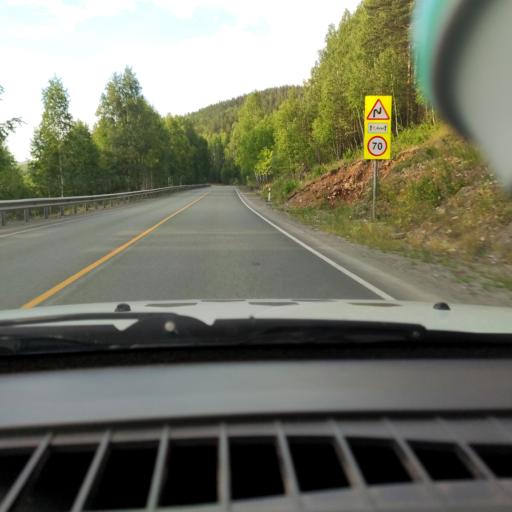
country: RU
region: Chelyabinsk
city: Turgoyak
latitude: 55.2425
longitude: 60.1951
